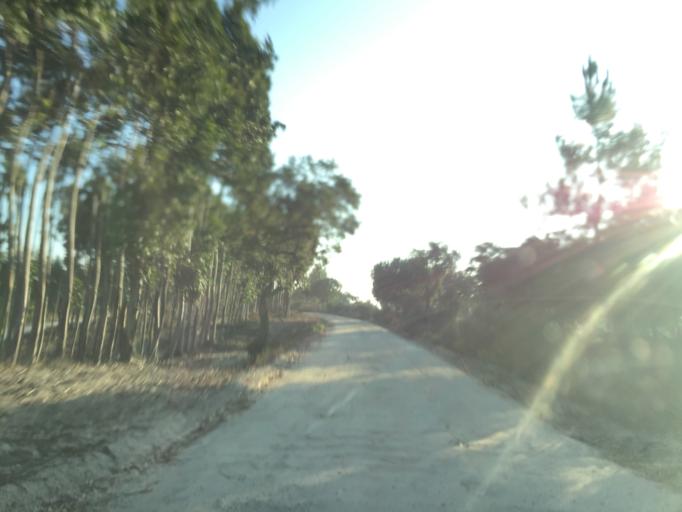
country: PT
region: Portalegre
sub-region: Ponte de Sor
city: Santo Andre
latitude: 39.1158
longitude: -8.3321
